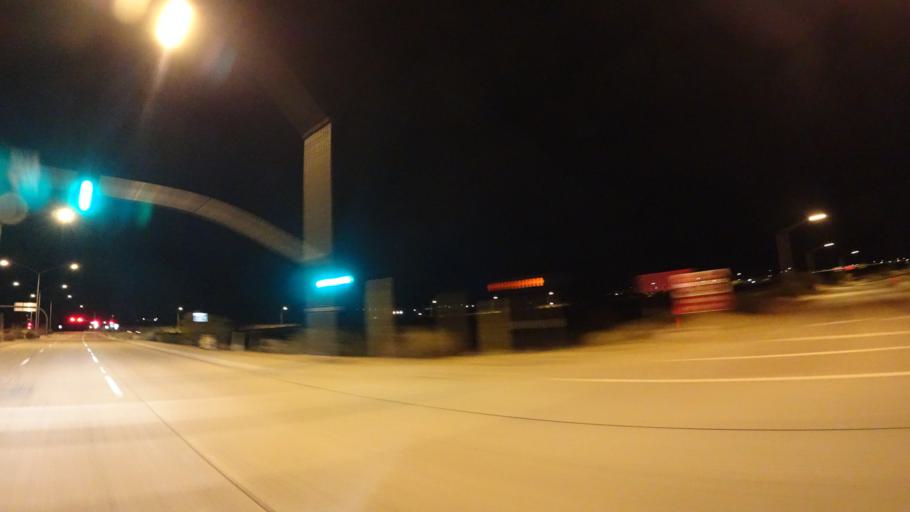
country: US
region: Arizona
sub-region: Maricopa County
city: Mesa
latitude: 33.4819
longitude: -111.7184
